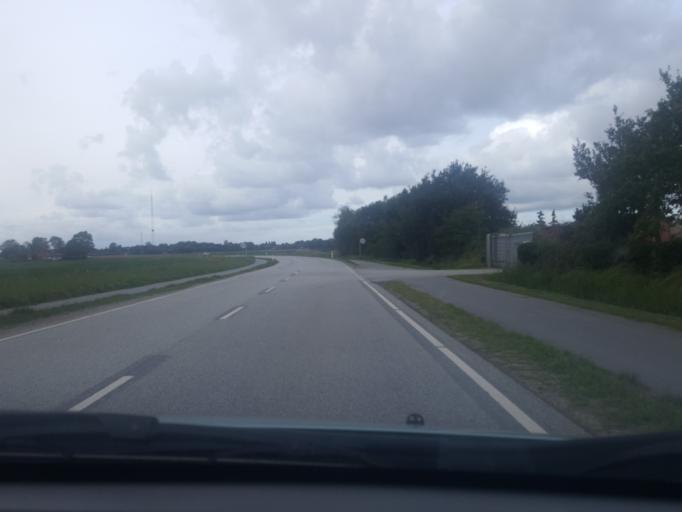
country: DK
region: Zealand
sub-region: Guldborgsund Kommune
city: Nykobing Falster
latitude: 54.6993
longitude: 11.9465
